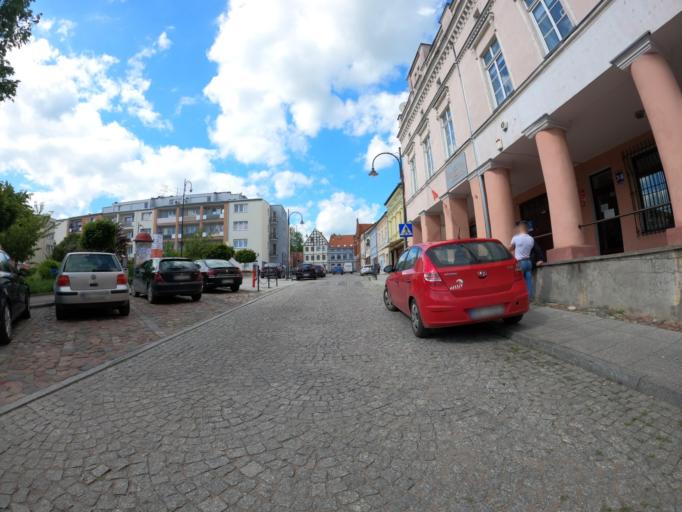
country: PL
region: Warmian-Masurian Voivodeship
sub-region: Powiat lidzbarski
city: Lidzbark Warminski
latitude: 54.1259
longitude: 20.5809
